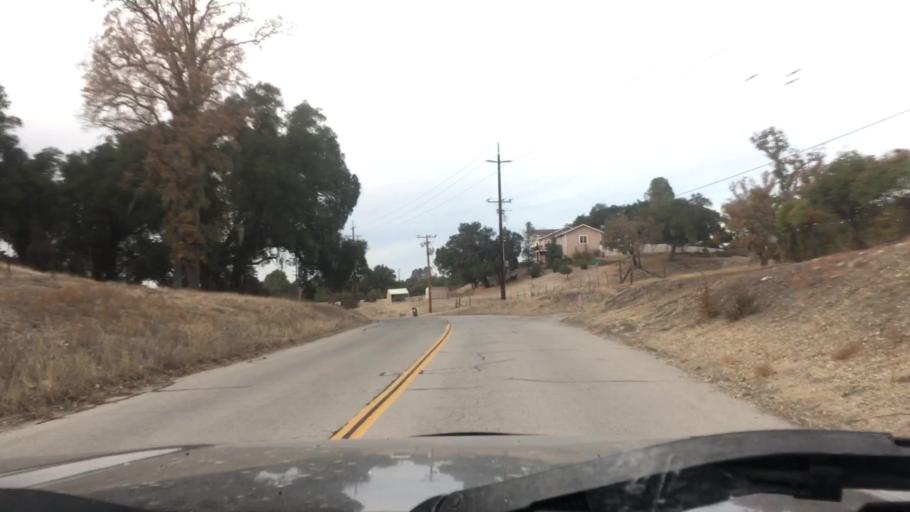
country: US
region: California
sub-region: San Luis Obispo County
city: Atascadero
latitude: 35.4437
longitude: -120.6456
